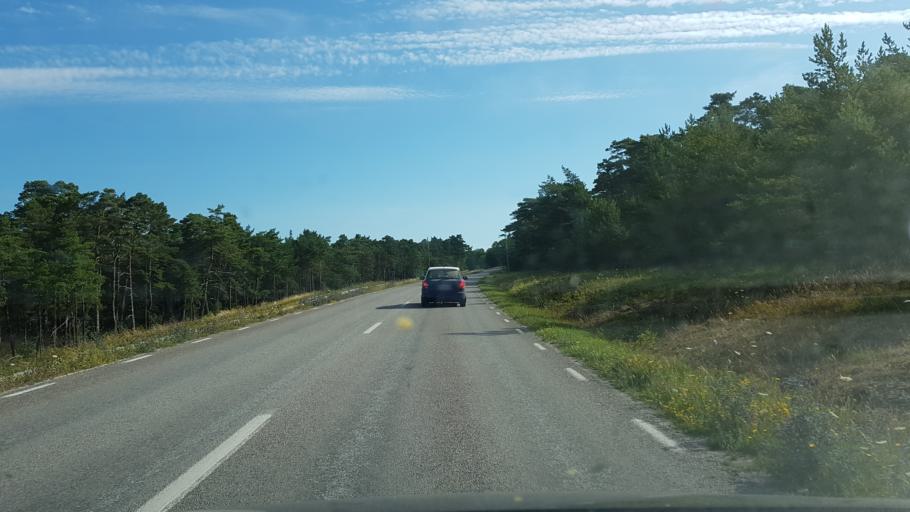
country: SE
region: Gotland
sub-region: Gotland
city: Visby
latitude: 57.7441
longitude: 18.4148
